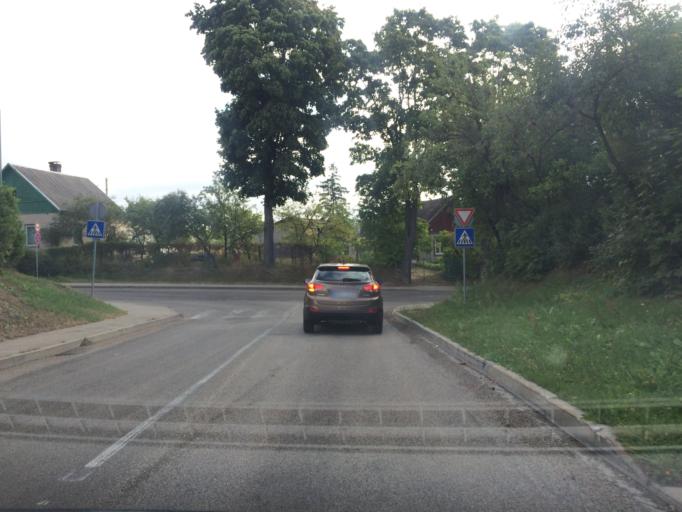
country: LV
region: Rezekne
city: Rezekne
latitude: 56.4936
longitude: 27.3430
